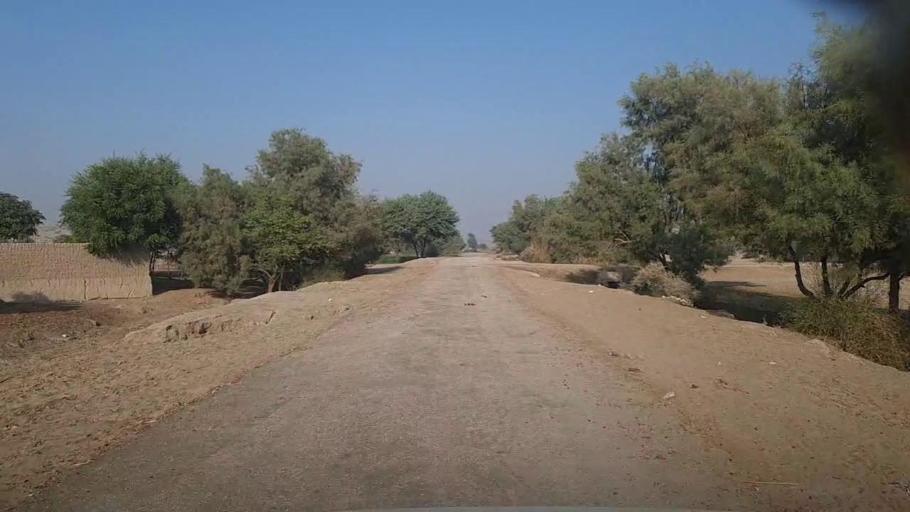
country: PK
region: Sindh
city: Kandiari
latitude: 26.7692
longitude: 68.5110
